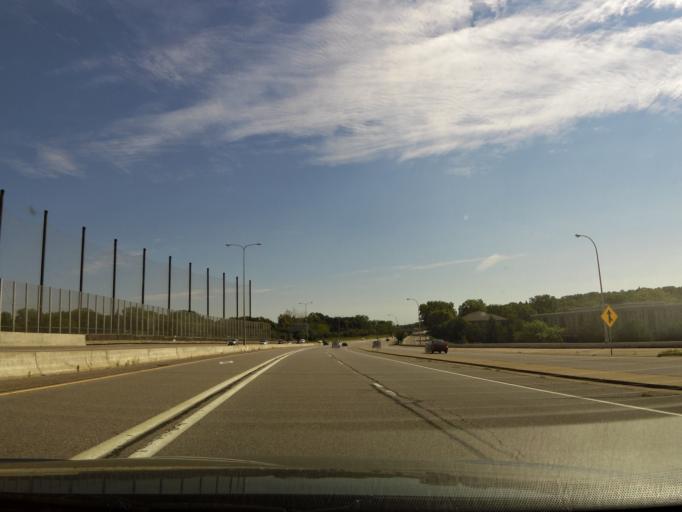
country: US
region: Minnesota
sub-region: Hennepin County
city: Saint Louis Park
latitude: 44.9738
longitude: -93.3898
